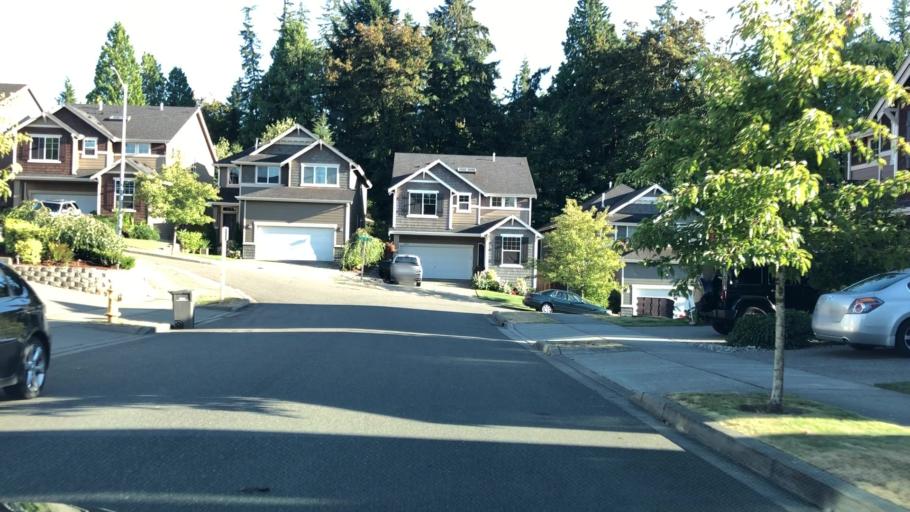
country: US
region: Washington
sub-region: Snohomish County
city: North Creek
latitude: 47.7889
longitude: -122.1765
